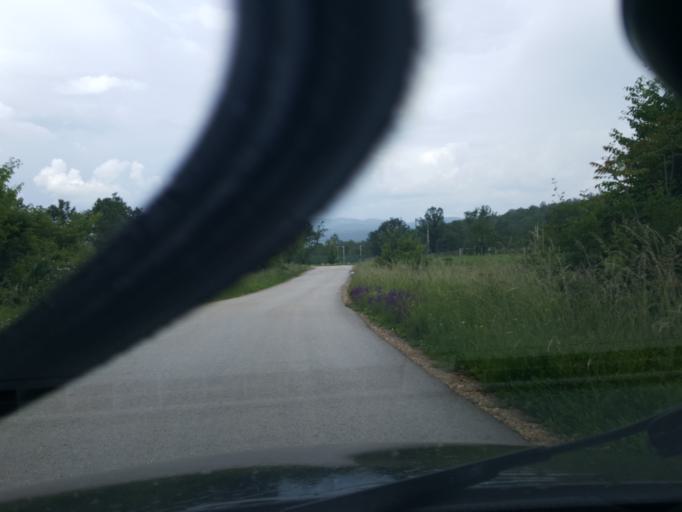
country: RS
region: Central Serbia
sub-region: Zajecarski Okrug
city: Boljevac
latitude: 43.8093
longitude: 21.8903
